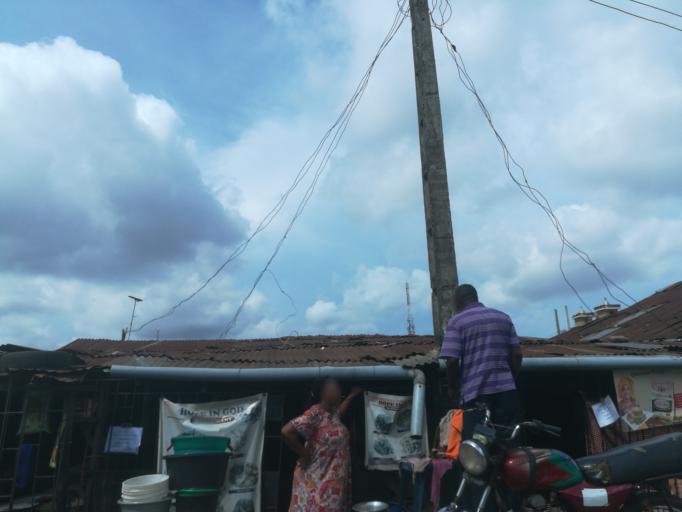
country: NG
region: Lagos
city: Somolu
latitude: 6.5314
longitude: 3.3827
